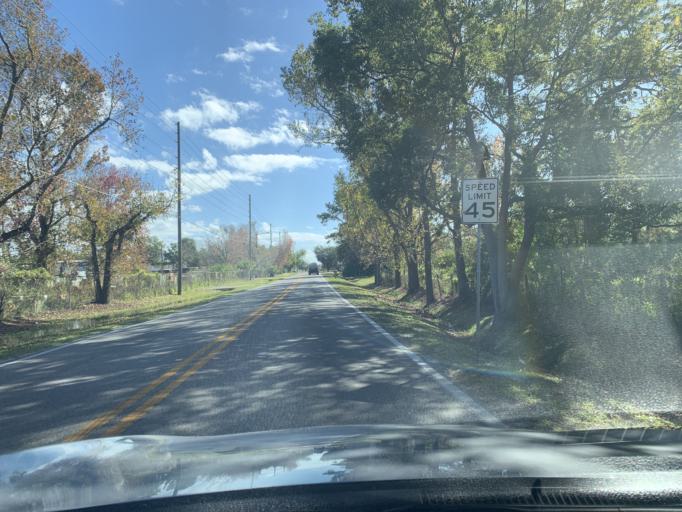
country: US
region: Florida
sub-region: Seminole County
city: Forest City
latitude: 28.6452
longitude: -81.4678
